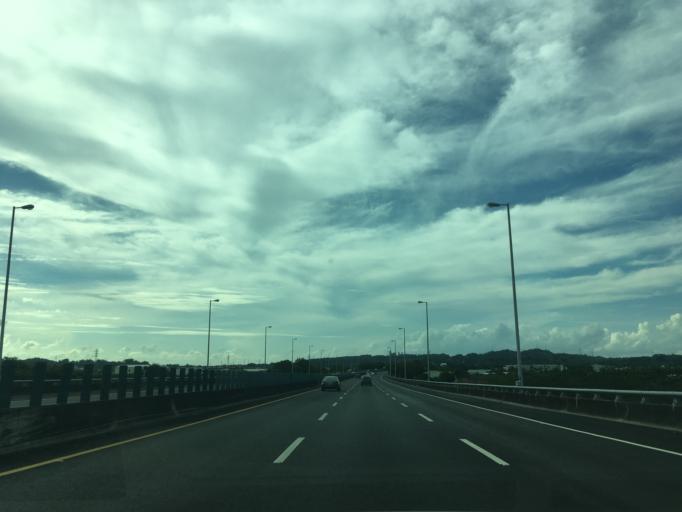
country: TW
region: Taiwan
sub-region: Chiayi
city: Jiayi Shi
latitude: 23.5053
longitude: 120.4901
